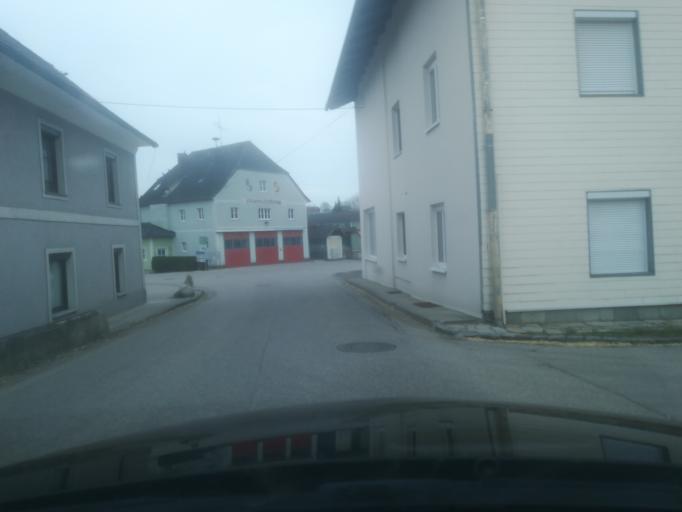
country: AT
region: Upper Austria
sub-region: Wels-Land
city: Gunskirchen
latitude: 48.0796
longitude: 13.9558
